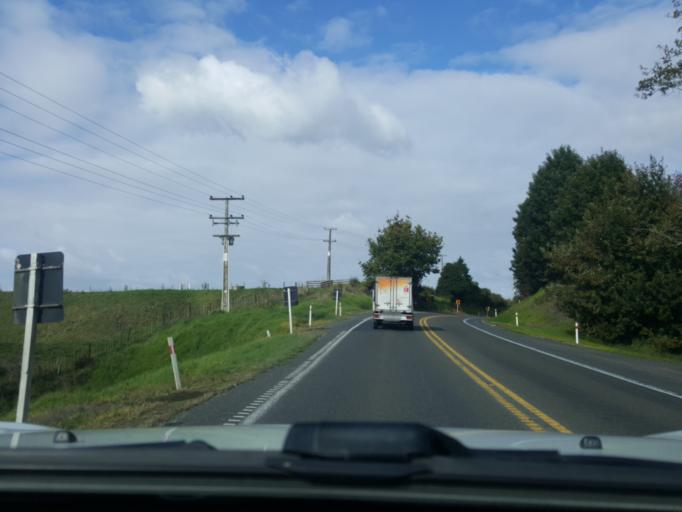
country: NZ
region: Bay of Plenty
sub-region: Tauranga City
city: Tauranga
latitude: -37.6688
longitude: 176.0201
